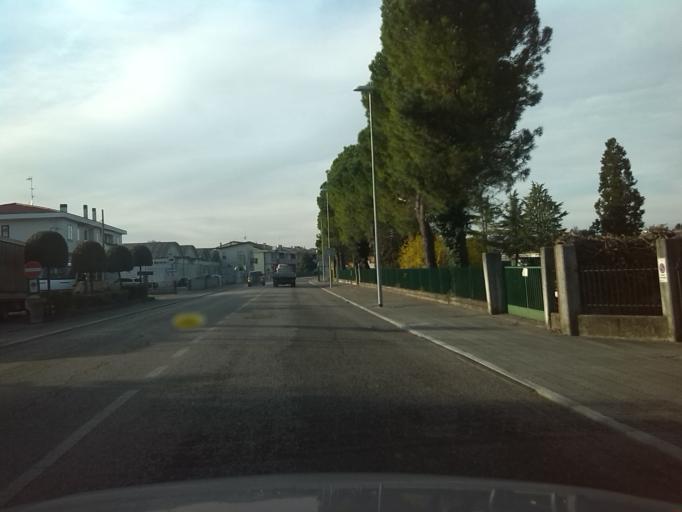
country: IT
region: Friuli Venezia Giulia
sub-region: Provincia di Udine
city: San Giovanni al Natisone
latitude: 45.9869
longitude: 13.3994
